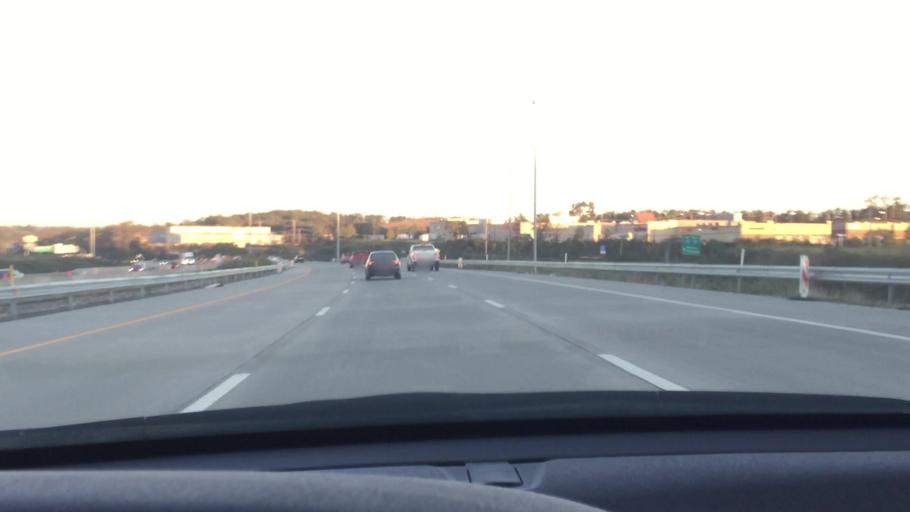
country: US
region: Pennsylvania
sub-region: Washington County
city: East Washington
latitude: 40.1832
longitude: -80.2262
